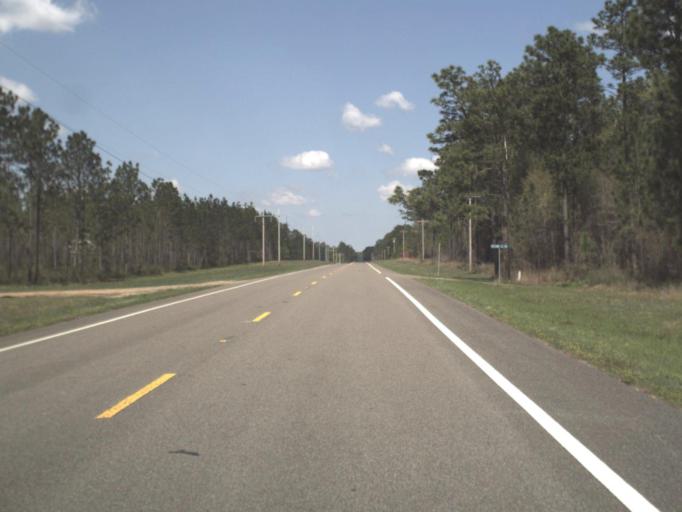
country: US
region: Florida
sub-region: Santa Rosa County
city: Point Baker
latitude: 30.8862
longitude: -86.9670
